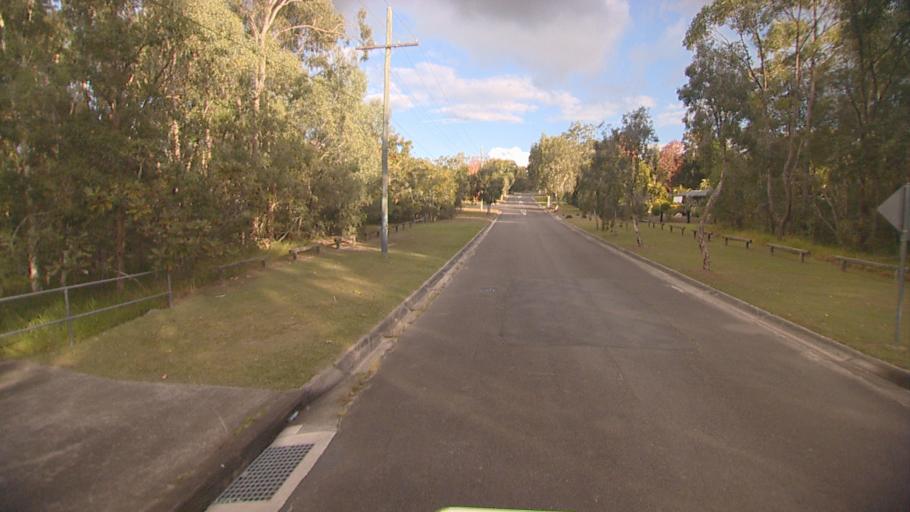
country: AU
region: Queensland
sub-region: Logan
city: Park Ridge South
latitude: -27.7025
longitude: 153.0205
